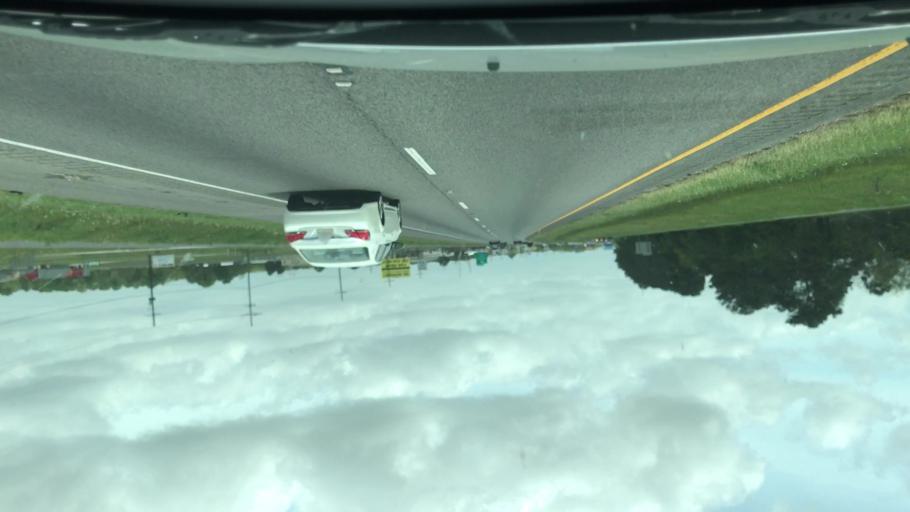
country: US
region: Louisiana
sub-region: Jefferson Davis Parish
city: Jennings
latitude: 30.2454
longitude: -92.6403
